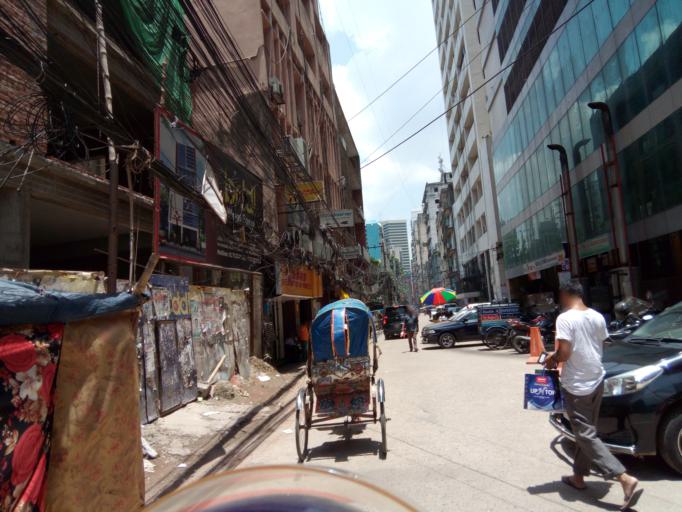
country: BD
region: Dhaka
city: Paltan
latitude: 23.7297
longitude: 90.4176
